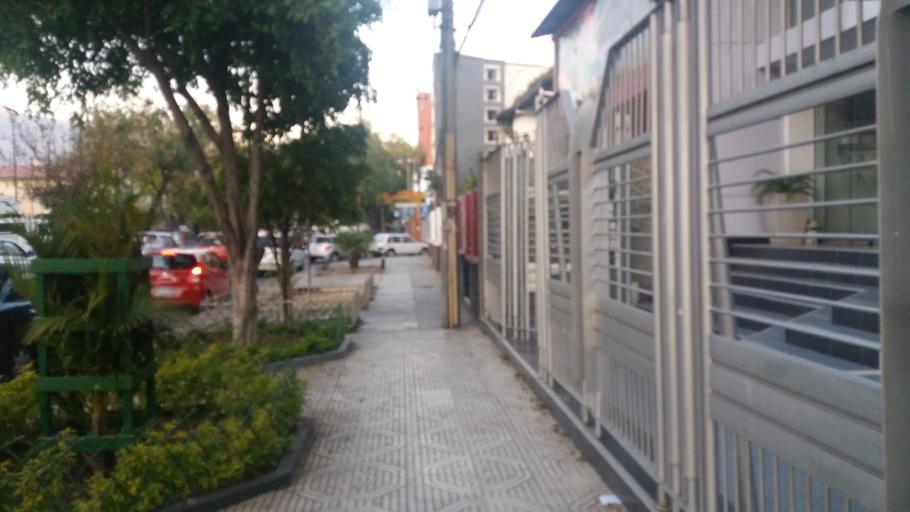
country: BO
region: Cochabamba
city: Cochabamba
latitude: -17.3821
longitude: -66.1585
